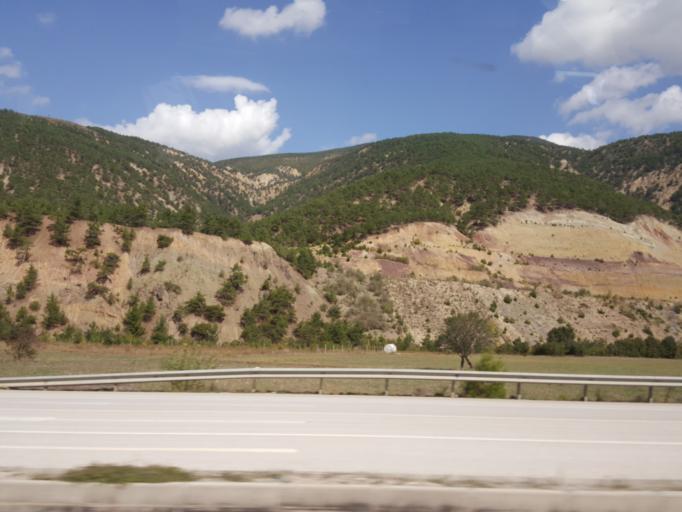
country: TR
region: Sivas
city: Dogansar
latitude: 40.3433
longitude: 37.5024
